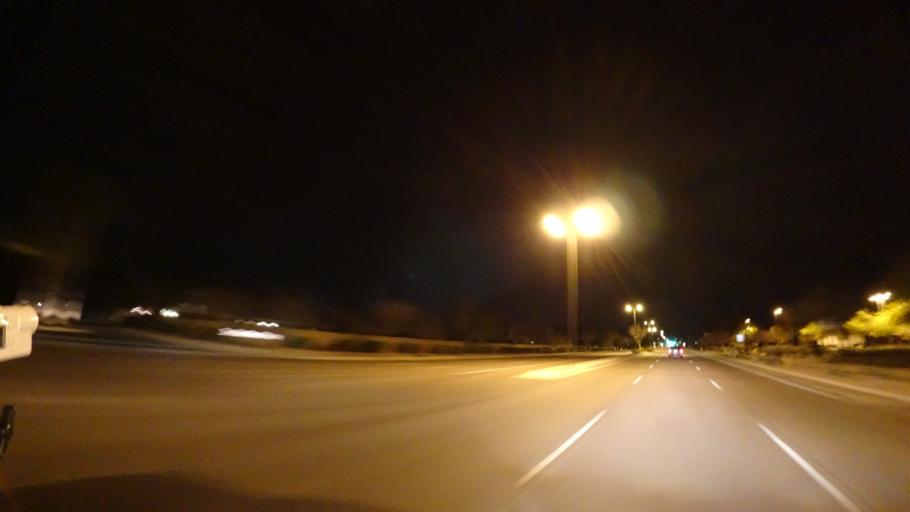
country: US
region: Arizona
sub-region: Maricopa County
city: Gilbert
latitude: 33.3355
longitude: -111.7837
